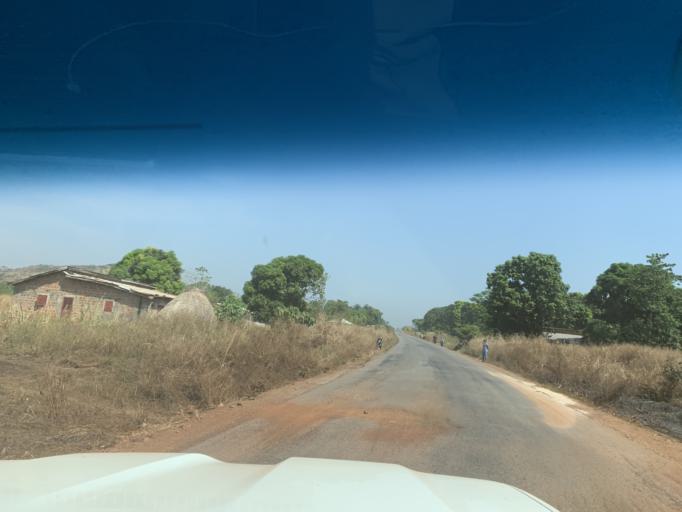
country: GN
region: Kindia
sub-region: Kindia
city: Kindia
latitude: 10.0171
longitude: -12.6829
